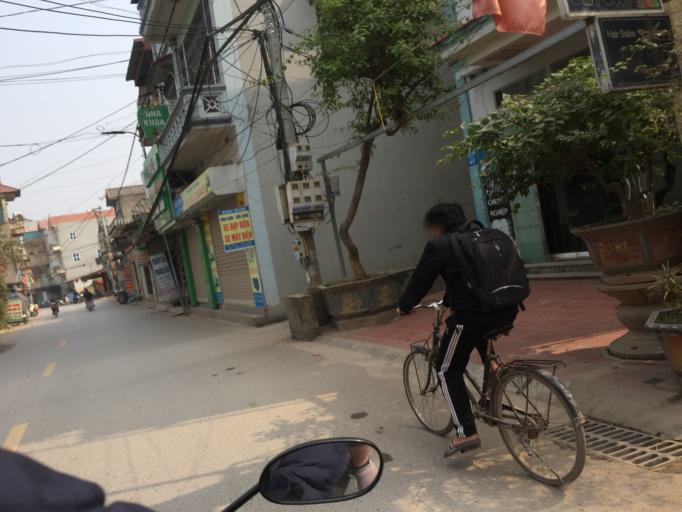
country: VN
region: Hung Yen
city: Van Giang
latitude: 20.9629
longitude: 105.9153
